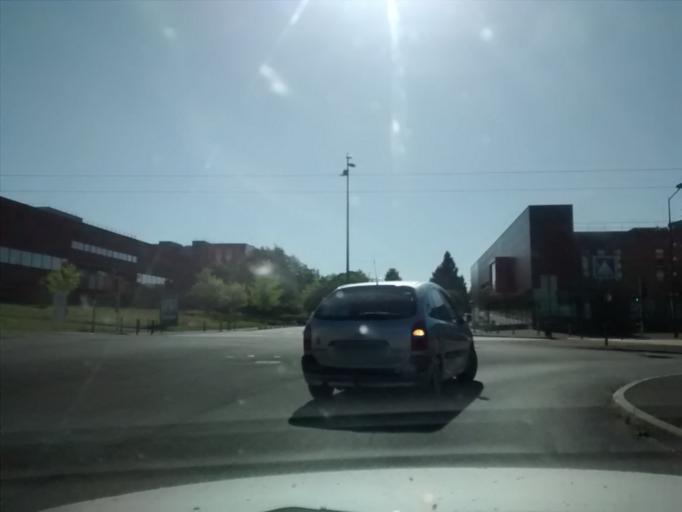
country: FR
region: Pays de la Loire
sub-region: Departement de la Sarthe
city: La Chapelle-Saint-Aubin
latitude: 48.0168
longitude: 0.1618
